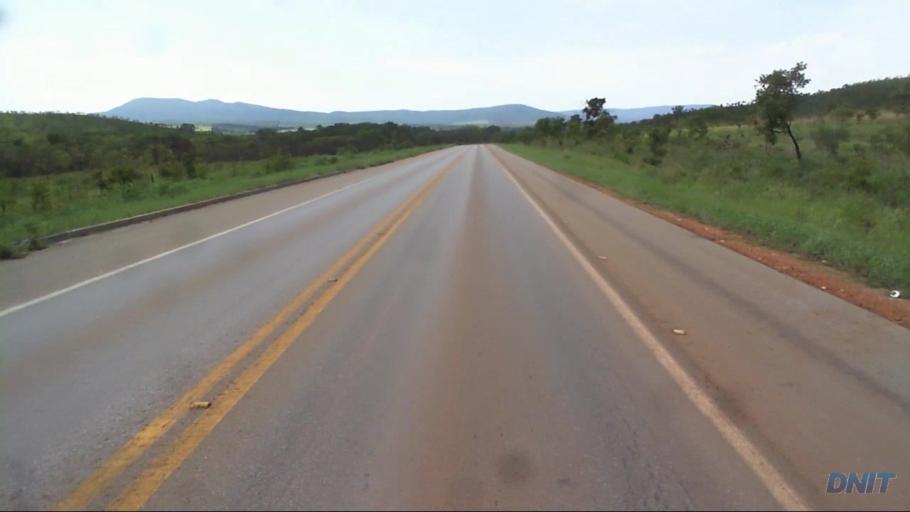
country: BR
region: Goias
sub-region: Barro Alto
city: Barro Alto
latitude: -15.1734
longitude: -48.7951
